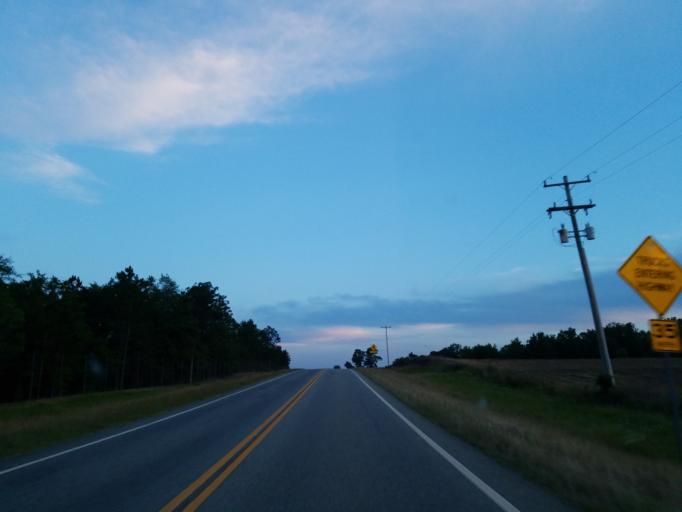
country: US
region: Georgia
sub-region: Worth County
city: Sylvester
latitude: 31.5951
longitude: -83.8302
